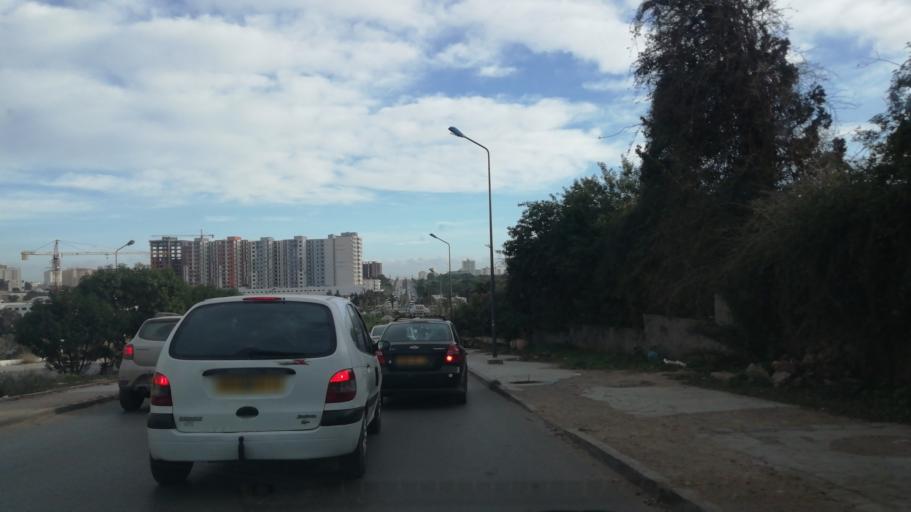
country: DZ
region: Oran
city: Bir el Djir
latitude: 35.7166
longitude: -0.5792
